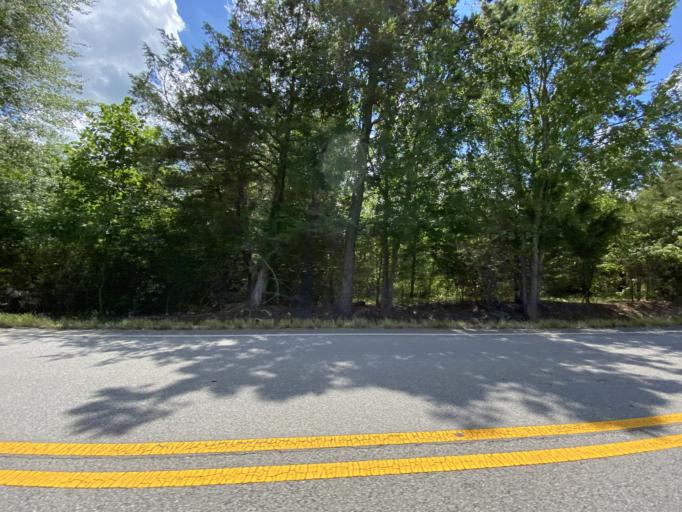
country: US
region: Alabama
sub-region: Lauderdale County
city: Underwood-Petersville
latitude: 34.9590
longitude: -87.8788
